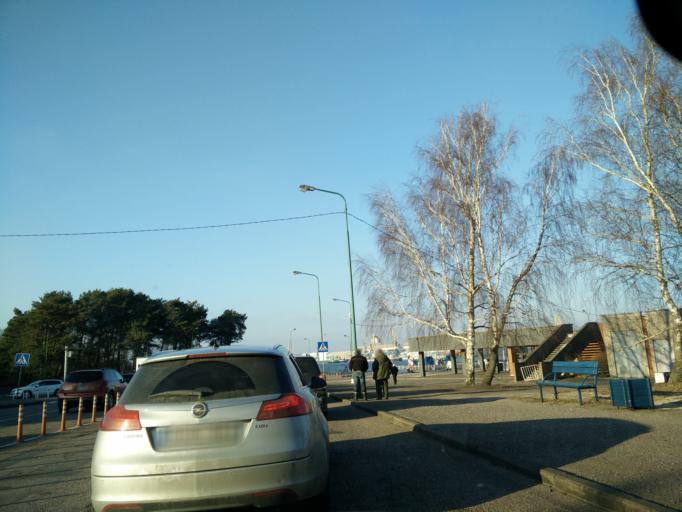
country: LT
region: Klaipedos apskritis
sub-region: Klaipeda
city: Klaipeda
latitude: 55.6848
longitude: 21.1299
